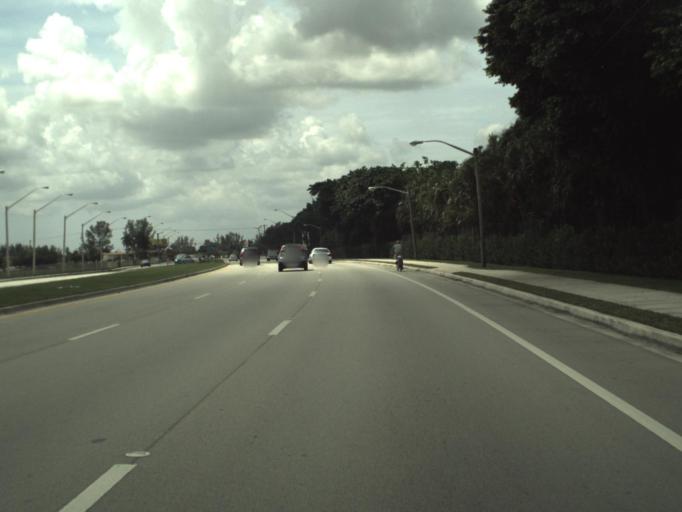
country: US
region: Florida
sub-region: Palm Beach County
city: Atlantis
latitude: 26.5922
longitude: -80.0939
